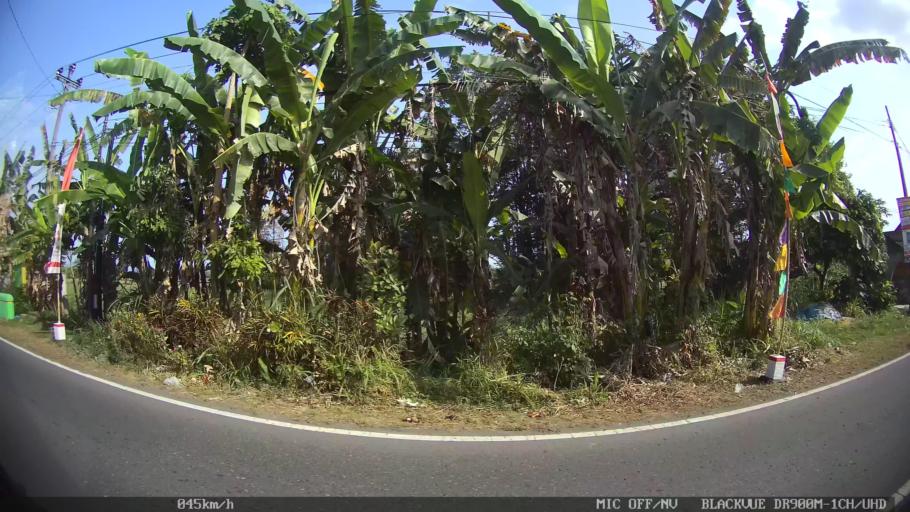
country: ID
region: Central Java
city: Candi Prambanan
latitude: -7.7294
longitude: 110.4649
